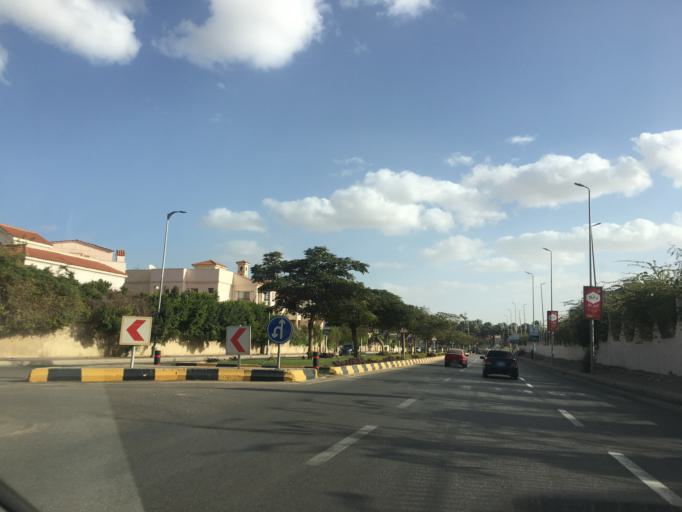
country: EG
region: Al Jizah
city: Awsim
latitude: 30.0243
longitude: 31.0031
